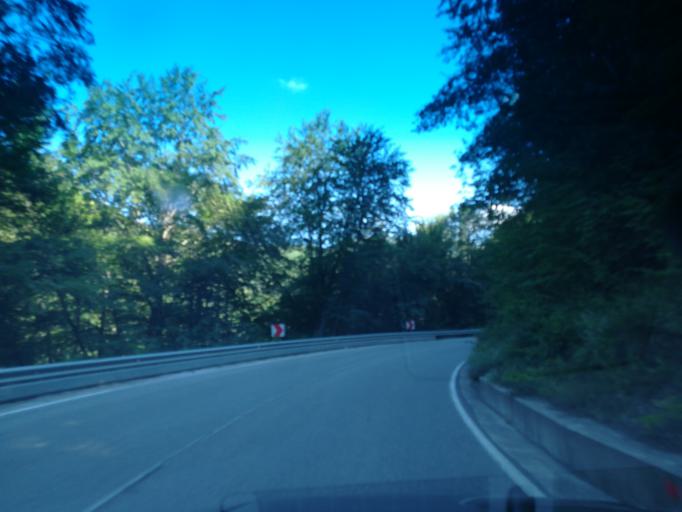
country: BG
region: Smolyan
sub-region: Obshtina Chepelare
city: Chepelare
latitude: 41.8119
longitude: 24.7051
